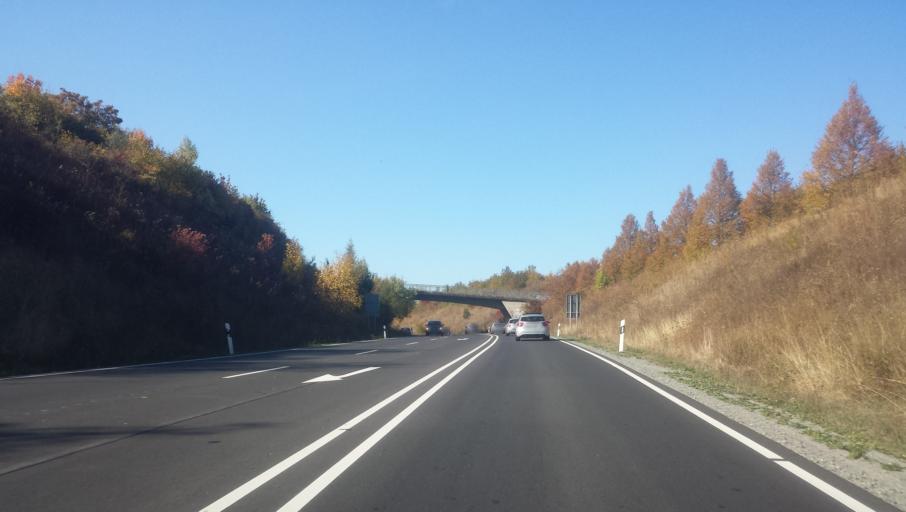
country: DE
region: Hesse
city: Ober-Ramstadt
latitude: 49.8222
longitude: 8.7387
